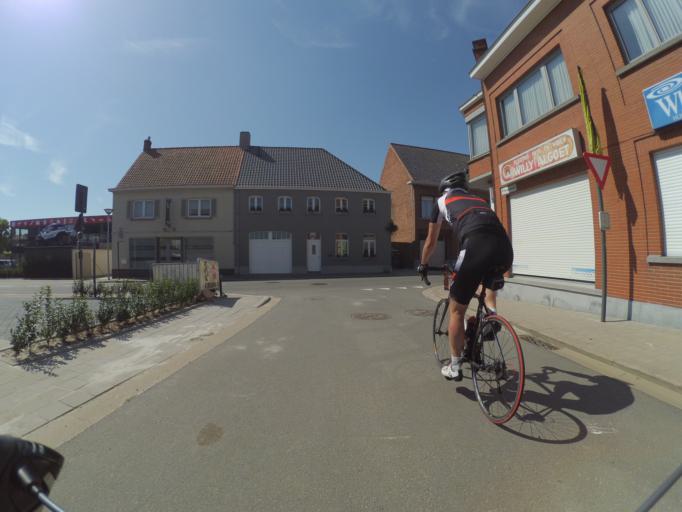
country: BE
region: Flanders
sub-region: Provincie West-Vlaanderen
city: Anzegem
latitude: 50.8533
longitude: 3.5078
